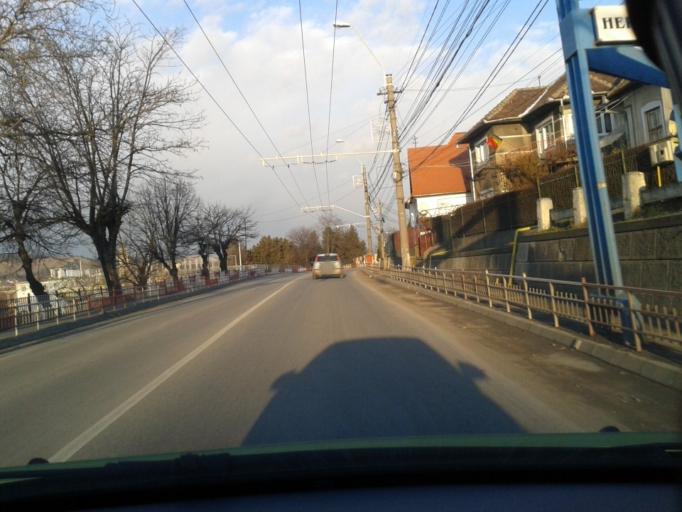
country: RO
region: Sibiu
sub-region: Municipiul Medias
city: Medias
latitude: 46.1583
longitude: 24.3459
